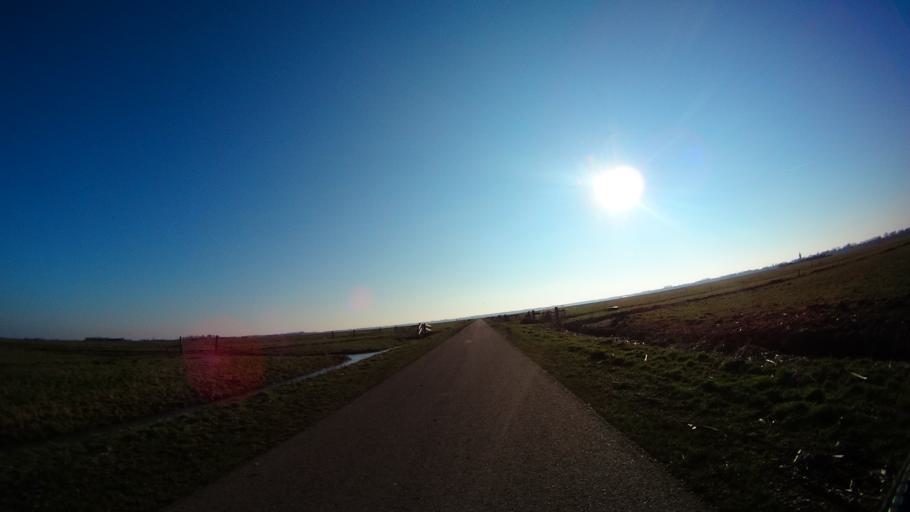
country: NL
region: Utrecht
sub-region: Gemeente Baarn
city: Baarn
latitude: 52.2606
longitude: 5.2894
